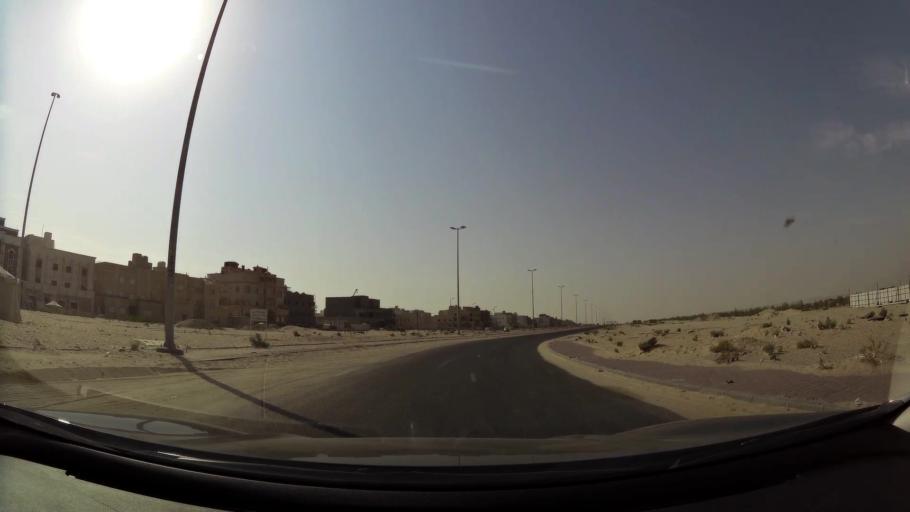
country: KW
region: Al Ahmadi
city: Al Wafrah
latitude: 28.7901
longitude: 48.0369
